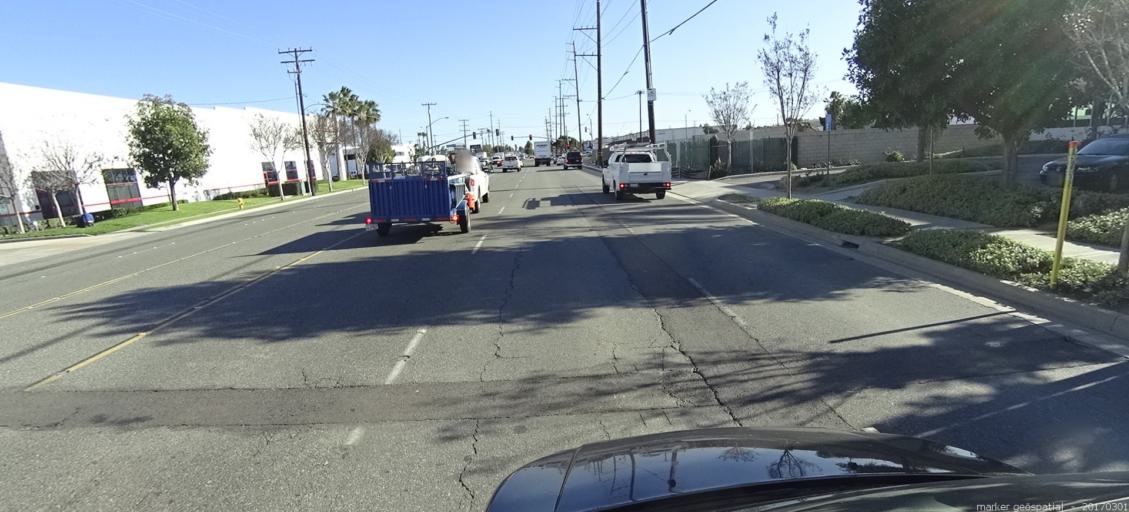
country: US
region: California
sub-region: Orange County
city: Placentia
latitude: 33.8557
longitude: -117.8591
